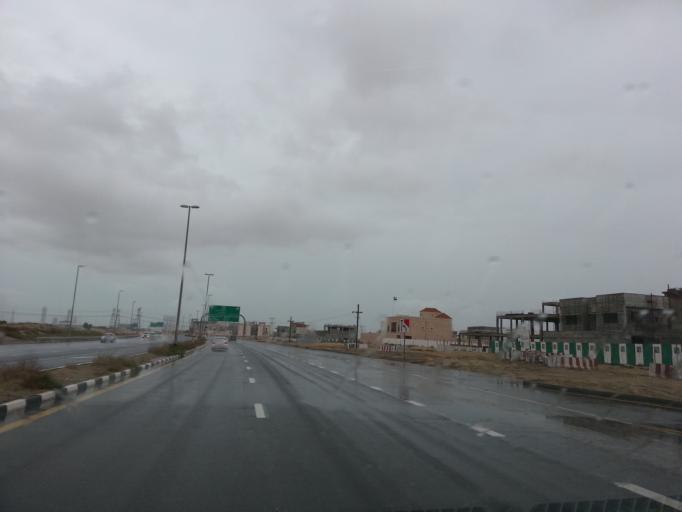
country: AE
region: Dubai
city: Dubai
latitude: 25.0675
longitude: 55.2192
